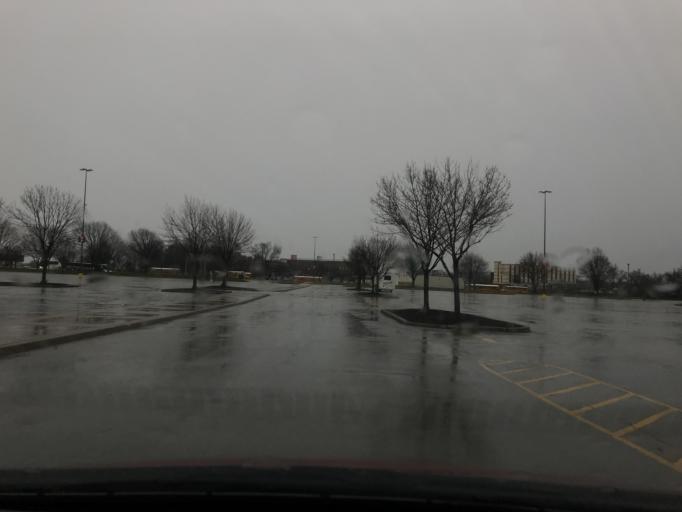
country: US
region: Kentucky
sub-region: Jefferson County
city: Audubon Park
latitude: 38.1970
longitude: -85.7427
